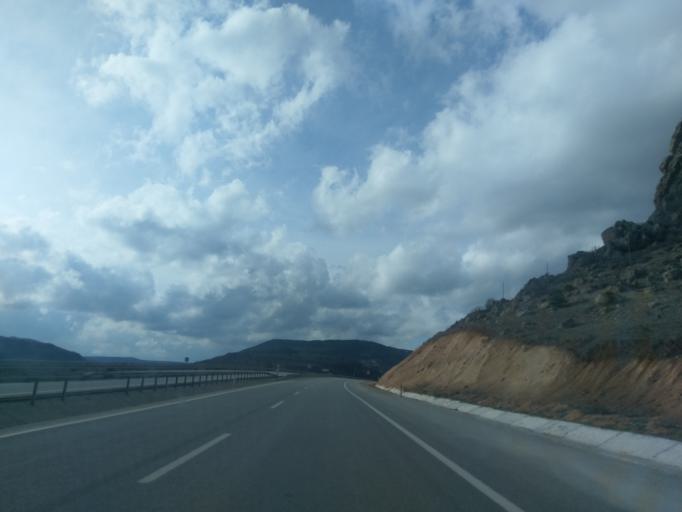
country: TR
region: Kuetahya
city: Sabuncu
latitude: 39.5739
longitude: 30.0994
